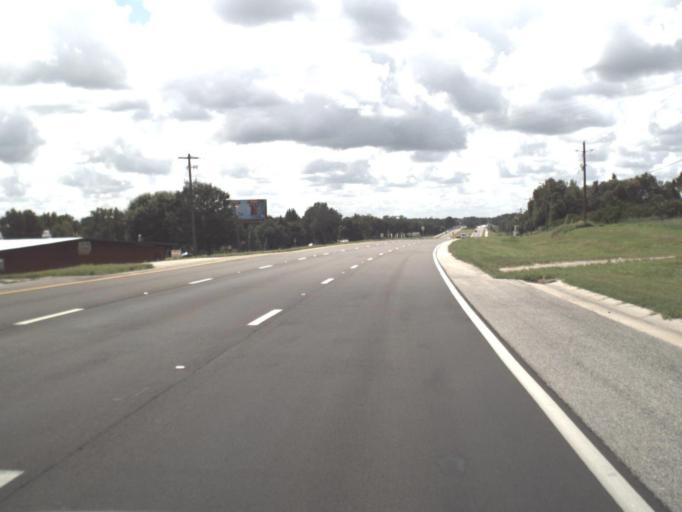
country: US
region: Florida
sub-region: Hardee County
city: Zolfo Springs
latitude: 27.5129
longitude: -81.8057
